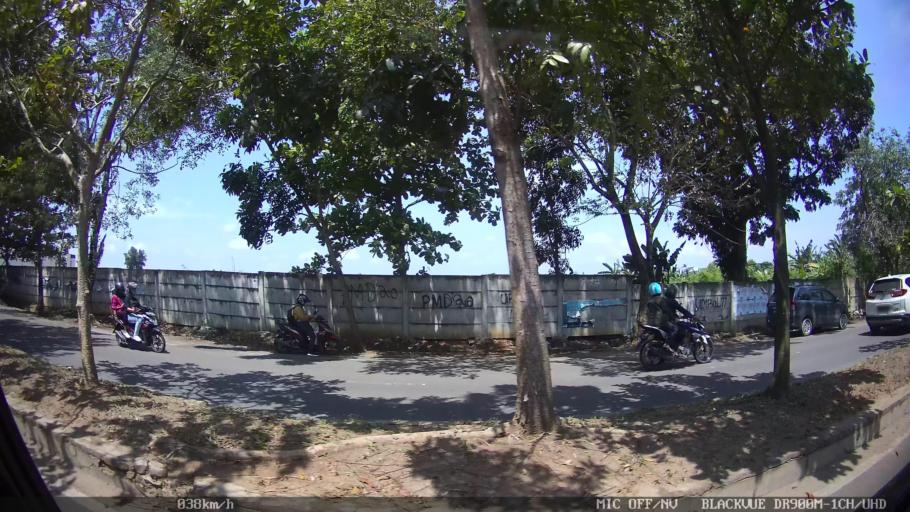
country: ID
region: Lampung
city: Kedaton
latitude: -5.3861
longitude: 105.2817
